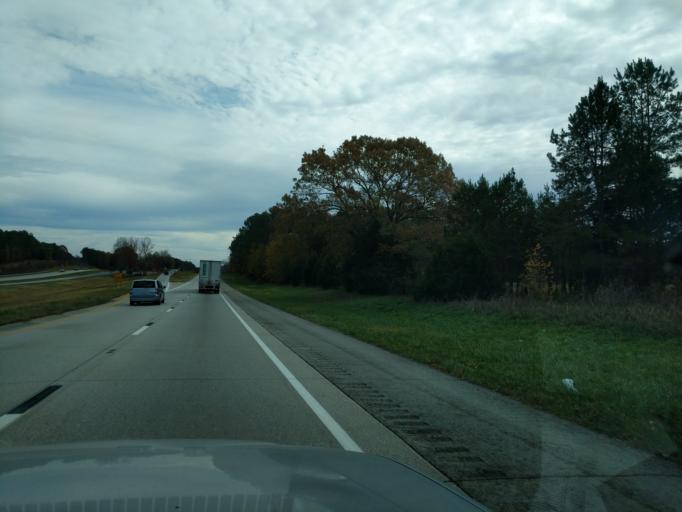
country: US
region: South Carolina
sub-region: Laurens County
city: Watts Mills
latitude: 34.5448
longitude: -81.9771
